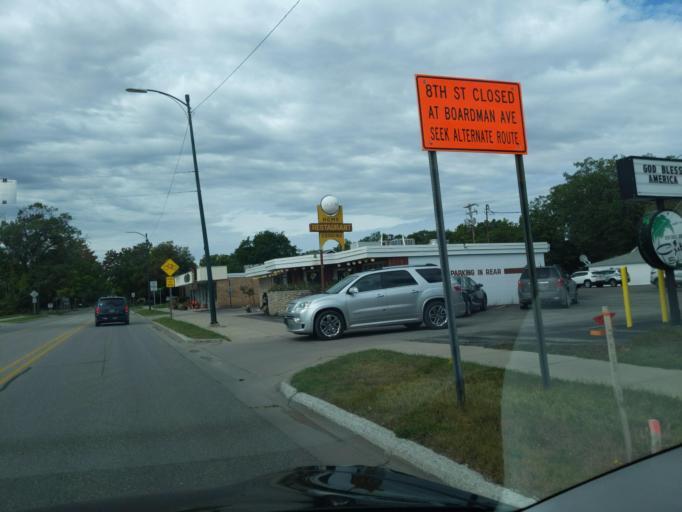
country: US
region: Michigan
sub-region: Grand Traverse County
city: Traverse City
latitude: 44.7587
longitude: -85.5958
